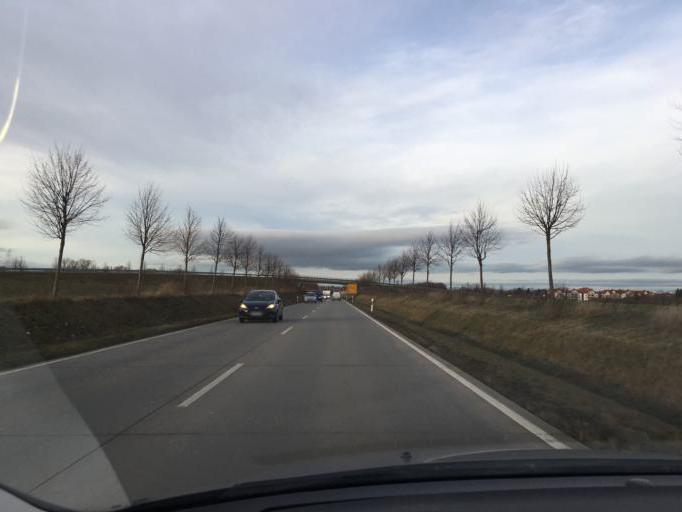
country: DE
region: Saxony
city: Grossposna
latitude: 51.2753
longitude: 12.4527
